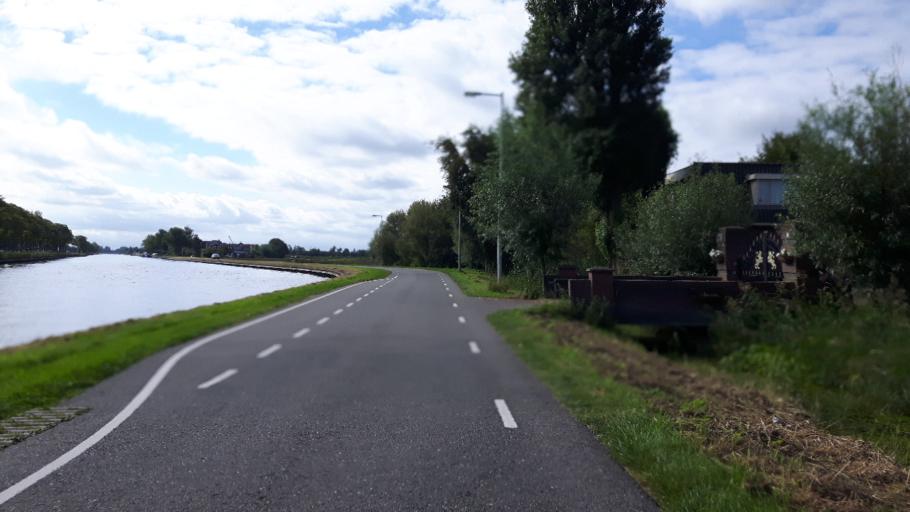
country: NL
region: North Holland
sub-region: Gemeente Landsmeer
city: Landsmeer
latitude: 52.4529
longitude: 4.9479
